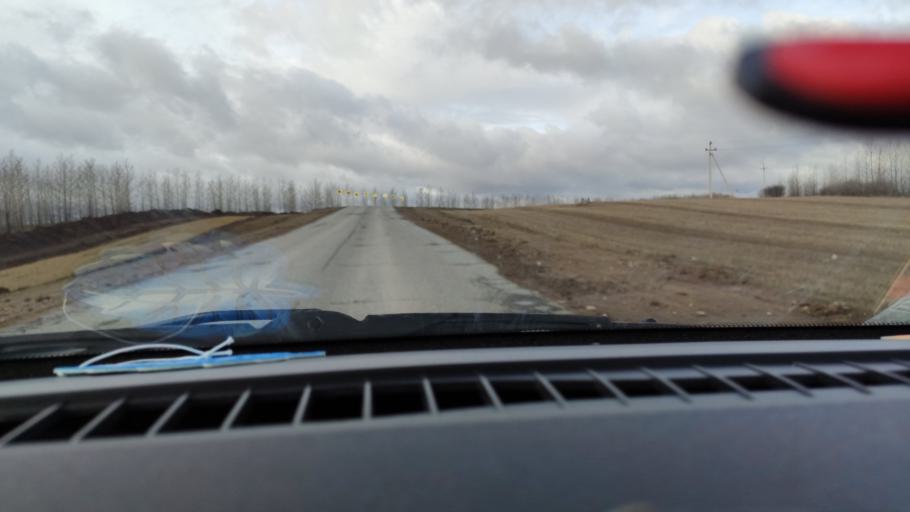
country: RU
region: Tatarstan
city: Russkiy Aktash
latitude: 55.0096
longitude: 51.7459
